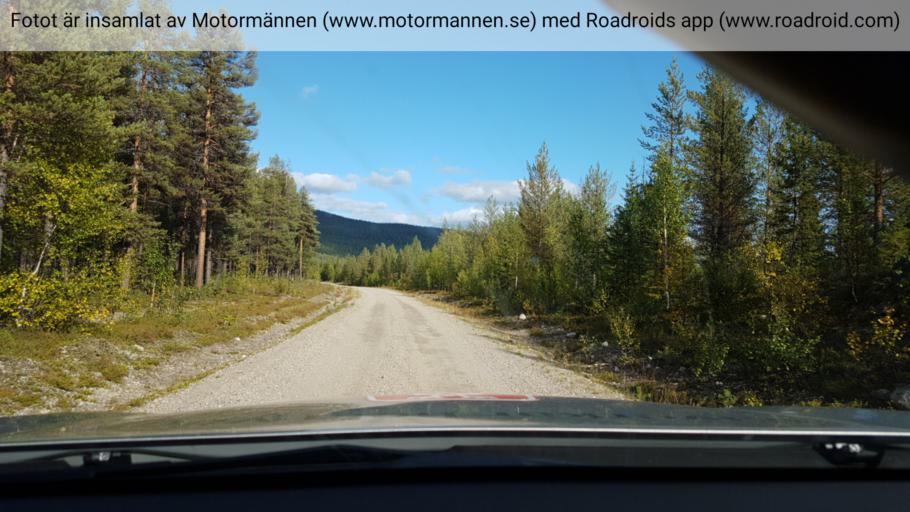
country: SE
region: Vaesterbotten
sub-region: Sorsele Kommun
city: Sorsele
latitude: 65.4669
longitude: 17.8416
